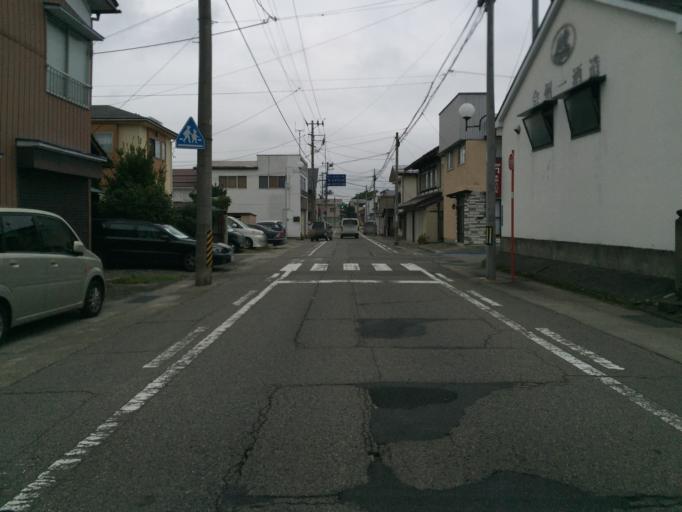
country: JP
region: Fukushima
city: Kitakata
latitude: 37.5015
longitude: 139.9359
